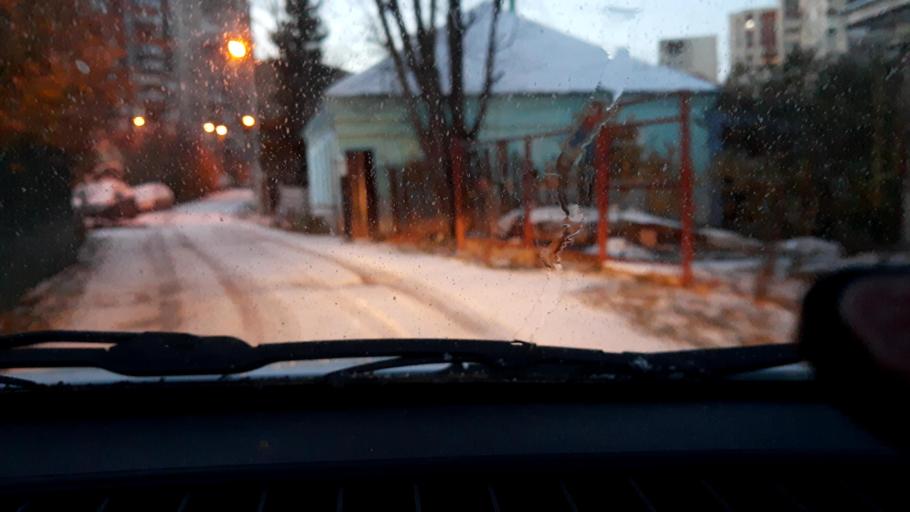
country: RU
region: Bashkortostan
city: Ufa
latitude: 54.7453
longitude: 55.9625
